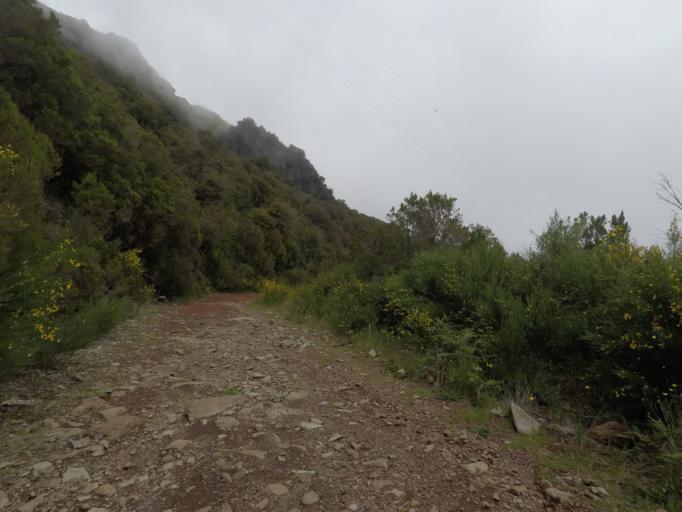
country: PT
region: Madeira
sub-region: Sao Vicente
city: Sao Vicente
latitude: 32.7691
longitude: -17.0674
